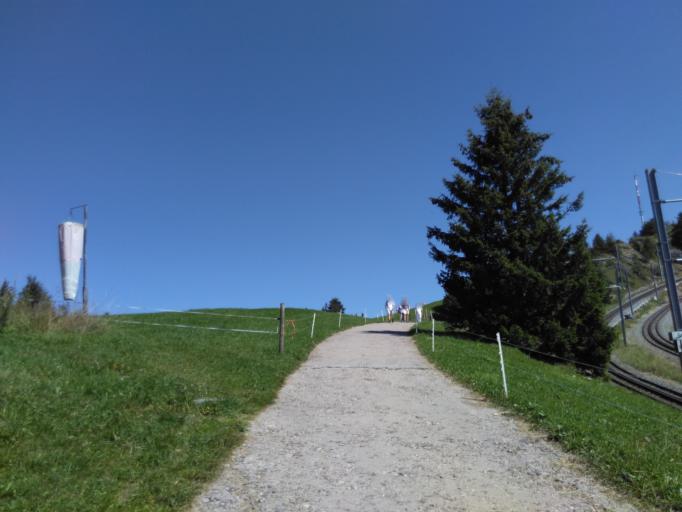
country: CH
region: Schwyz
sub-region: Bezirk Kuessnacht
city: Kussnacht
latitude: 47.0544
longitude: 8.4747
